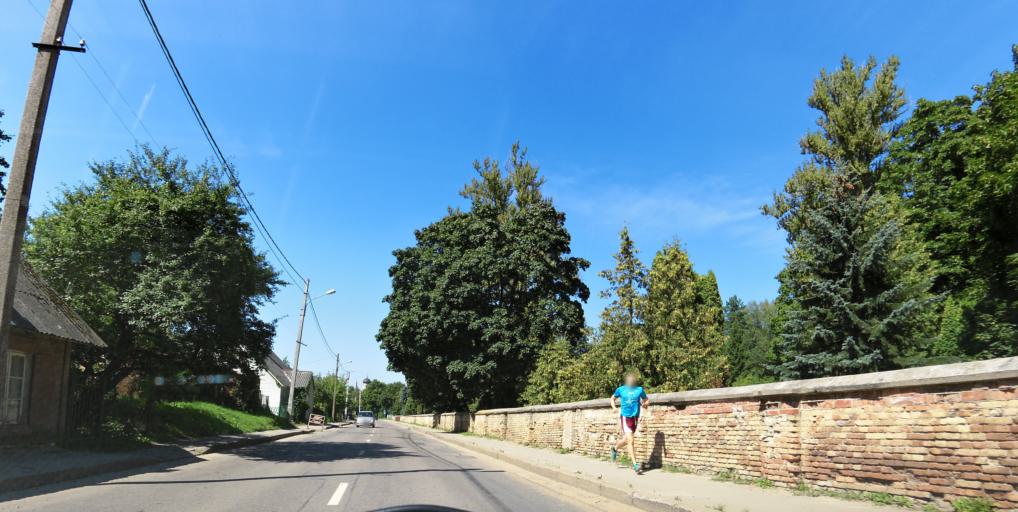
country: LT
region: Vilnius County
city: Rasos
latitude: 54.6638
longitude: 25.2956
